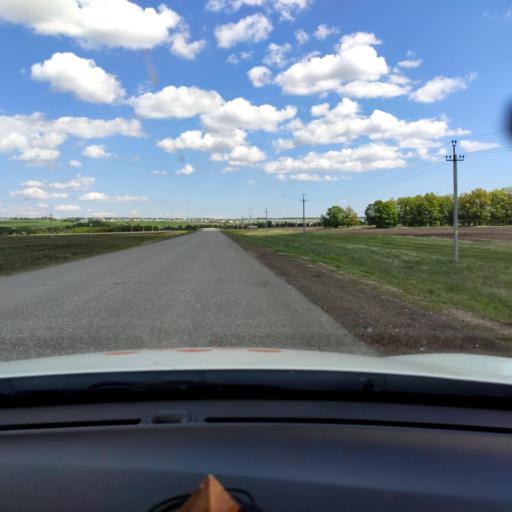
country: RU
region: Tatarstan
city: Kuybyshevskiy Zaton
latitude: 55.1693
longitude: 49.2149
